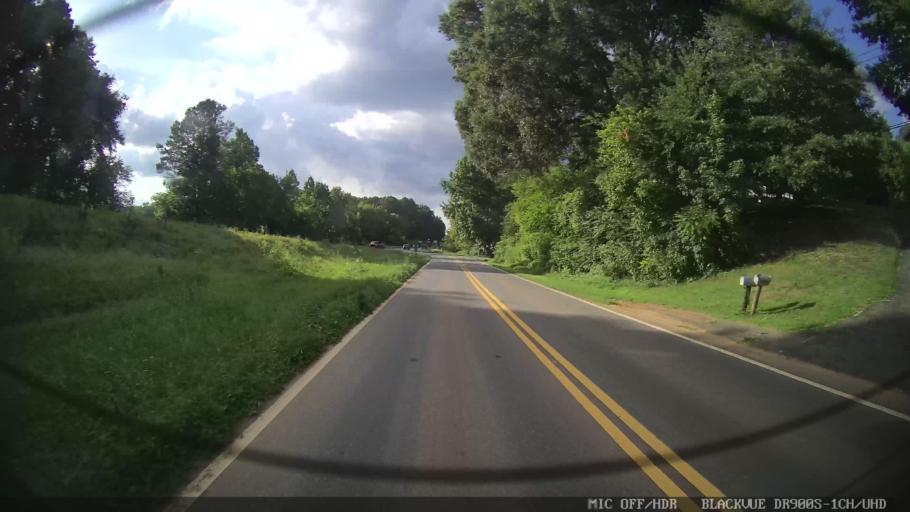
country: US
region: Georgia
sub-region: Bartow County
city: Cartersville
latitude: 34.2585
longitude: -84.8578
